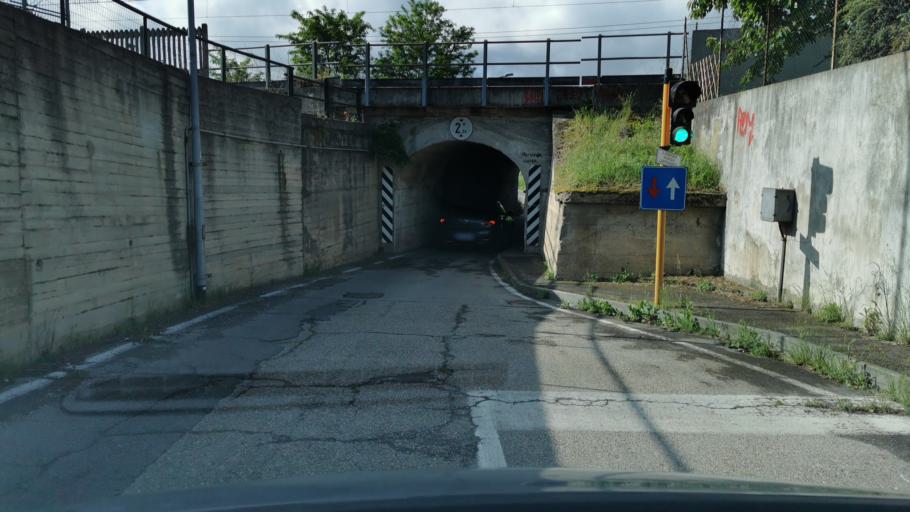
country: IT
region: Piedmont
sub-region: Provincia di Torino
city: Cambiano
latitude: 44.9664
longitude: 7.7812
